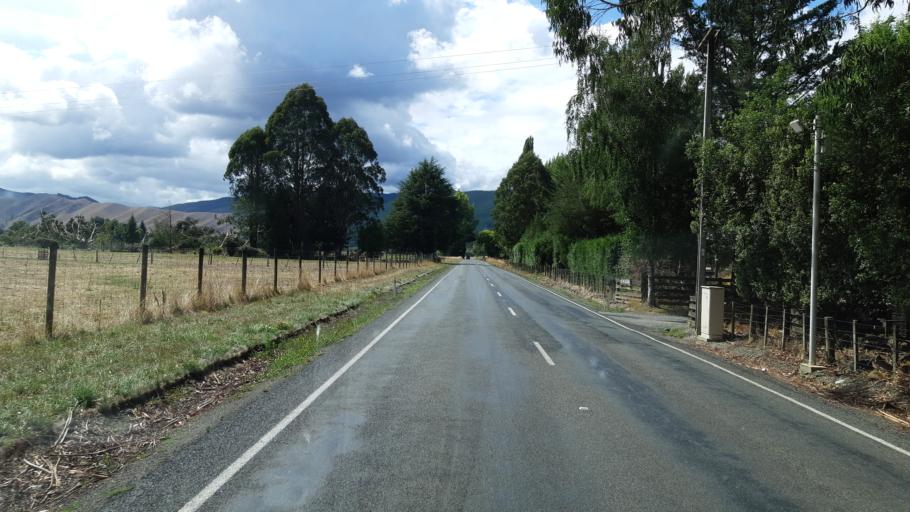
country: NZ
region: Tasman
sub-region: Tasman District
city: Wakefield
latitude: -41.4526
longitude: 172.8207
